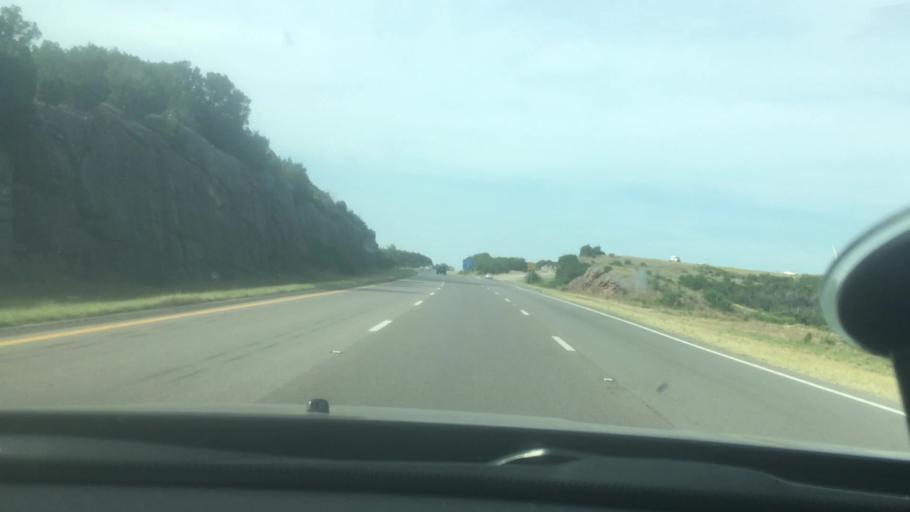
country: US
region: Oklahoma
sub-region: Murray County
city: Davis
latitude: 34.4294
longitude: -97.1332
